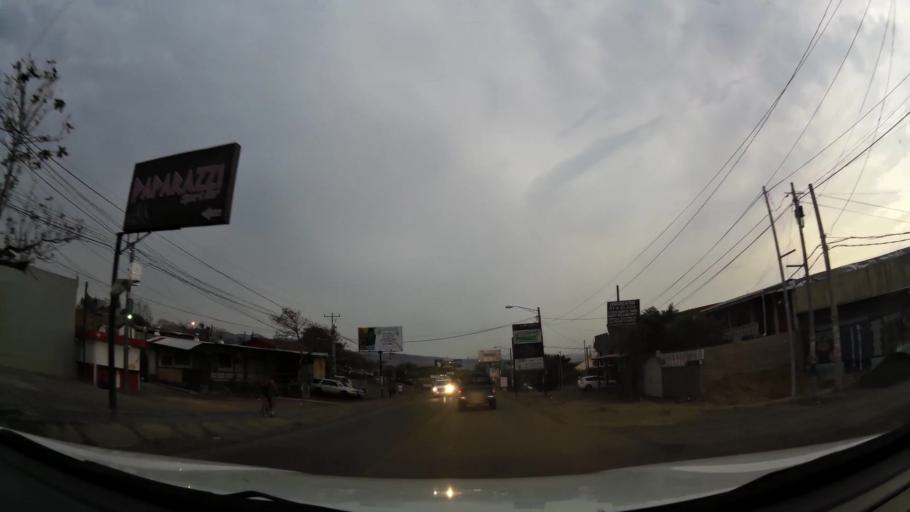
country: NI
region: Esteli
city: Esteli
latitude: 13.0692
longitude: -86.3502
